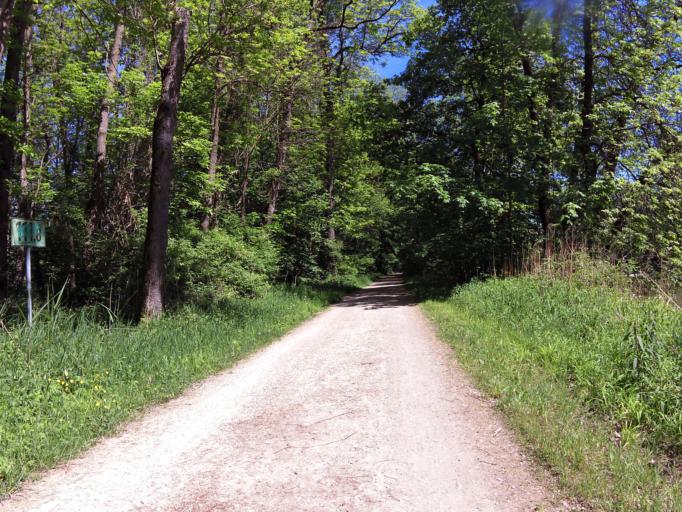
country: DE
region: Bavaria
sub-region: Upper Bavaria
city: Marzling
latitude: 48.4063
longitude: 11.7717
